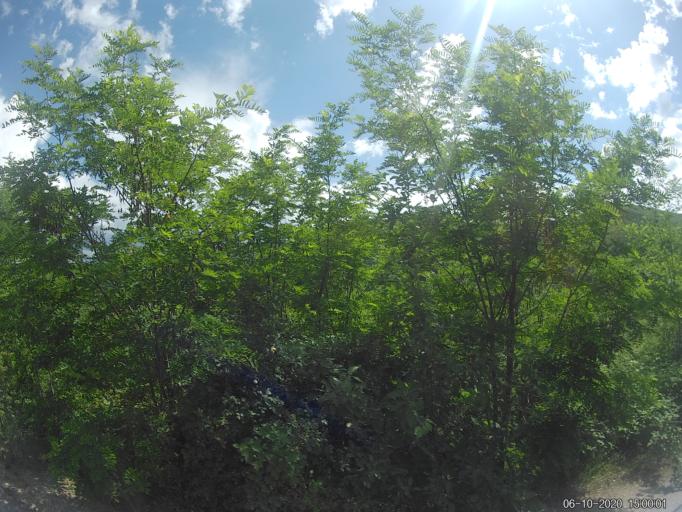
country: XK
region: Ferizaj
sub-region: Komuna e Shtimes
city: Shtime
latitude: 42.4128
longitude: 21.0285
